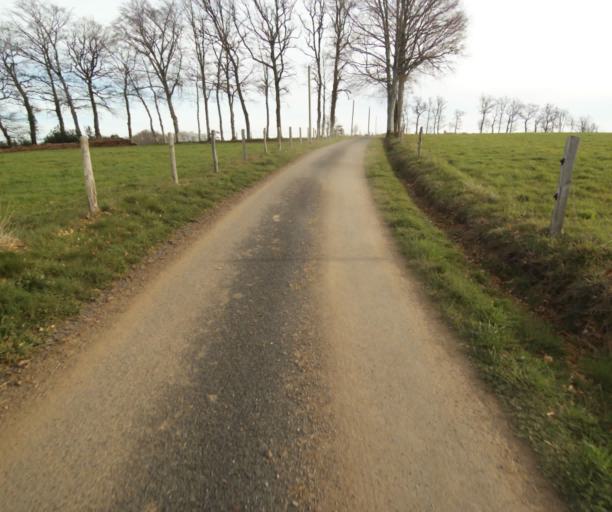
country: FR
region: Limousin
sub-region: Departement de la Correze
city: Chamboulive
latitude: 45.4539
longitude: 1.7554
